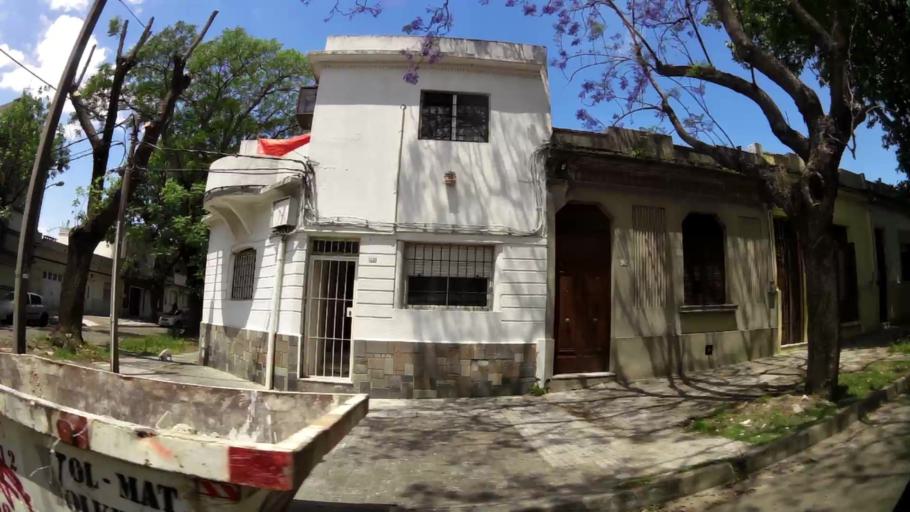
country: UY
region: Montevideo
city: Montevideo
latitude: -34.8681
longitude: -56.1899
